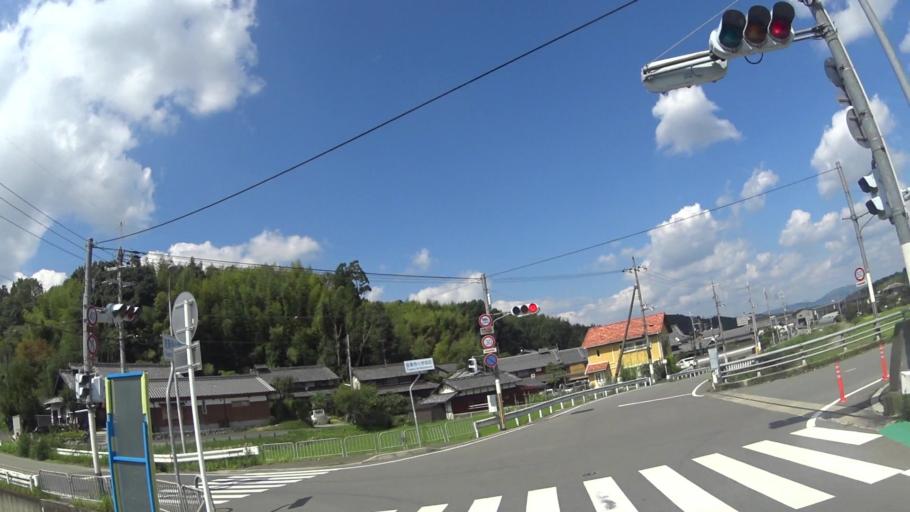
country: JP
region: Kyoto
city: Tanabe
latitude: 34.7845
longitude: 135.7524
